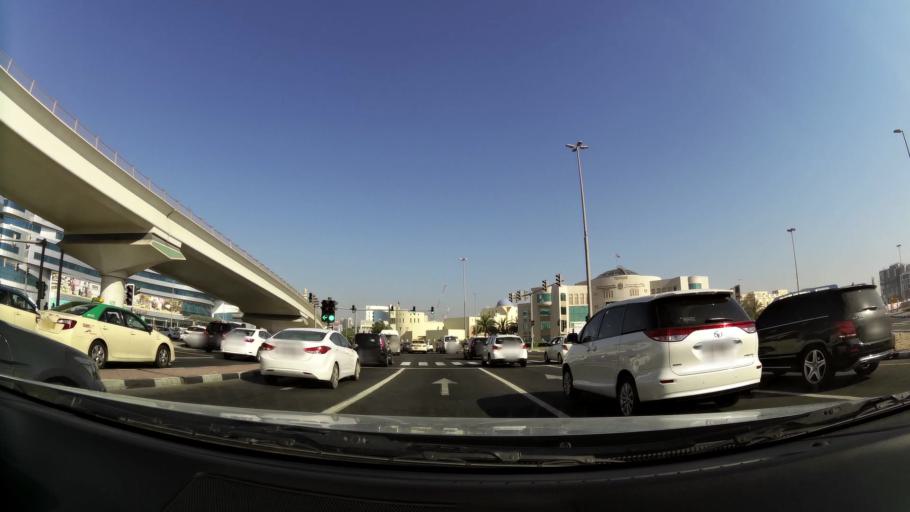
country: AE
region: Ash Shariqah
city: Sharjah
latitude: 25.2522
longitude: 55.3104
